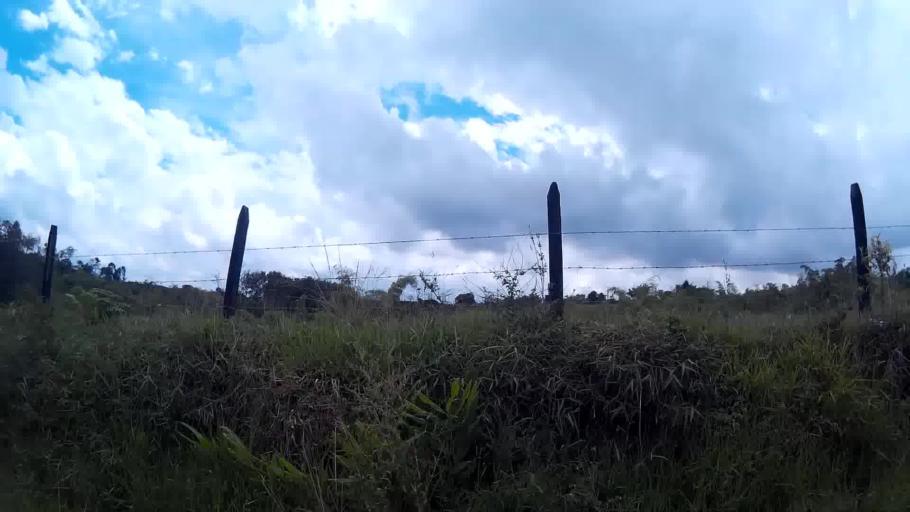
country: CO
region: Valle del Cauca
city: Ulloa
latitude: 4.7225
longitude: -75.6957
